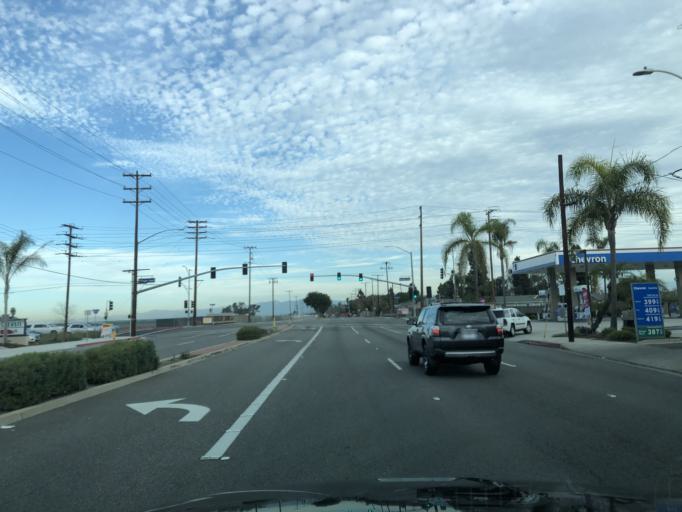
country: US
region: California
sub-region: Orange County
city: Westminster
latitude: 33.7291
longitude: -118.0416
